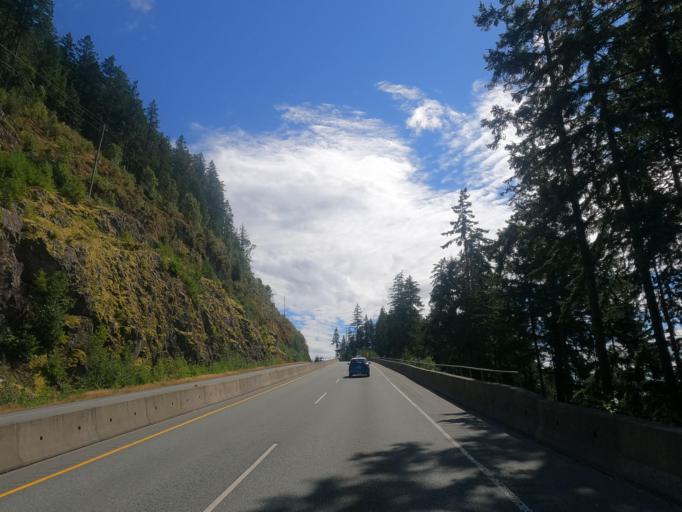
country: CA
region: British Columbia
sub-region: Greater Vancouver Regional District
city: Bowen Island
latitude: 49.3799
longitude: -123.2652
